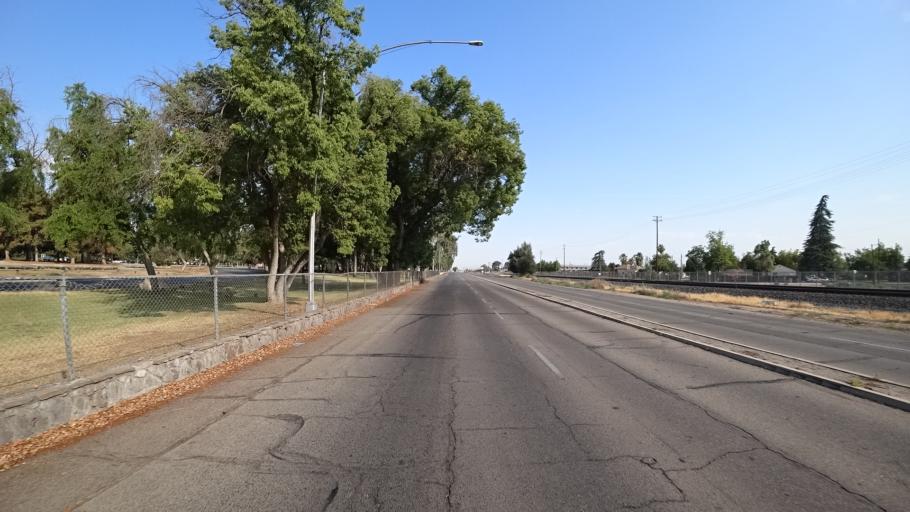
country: US
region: California
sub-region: Fresno County
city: Fresno
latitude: 36.7542
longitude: -119.8182
